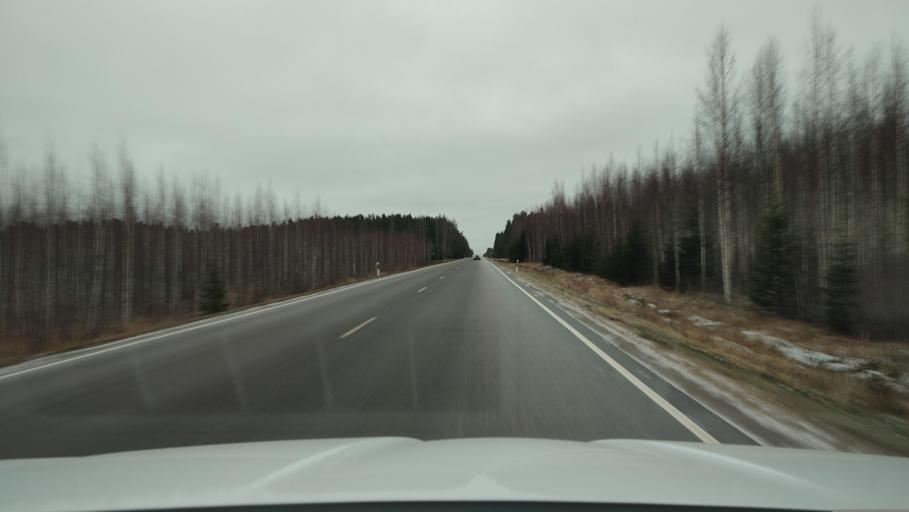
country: FI
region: Ostrobothnia
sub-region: Sydosterbotten
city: Naerpes
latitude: 62.5671
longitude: 21.4842
